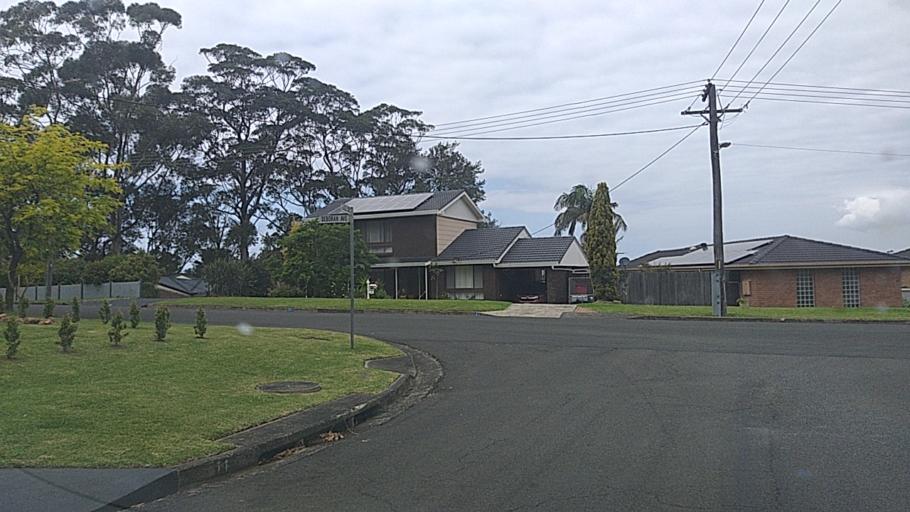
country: AU
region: New South Wales
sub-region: Wollongong
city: Bulli
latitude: -34.3139
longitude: 150.9118
